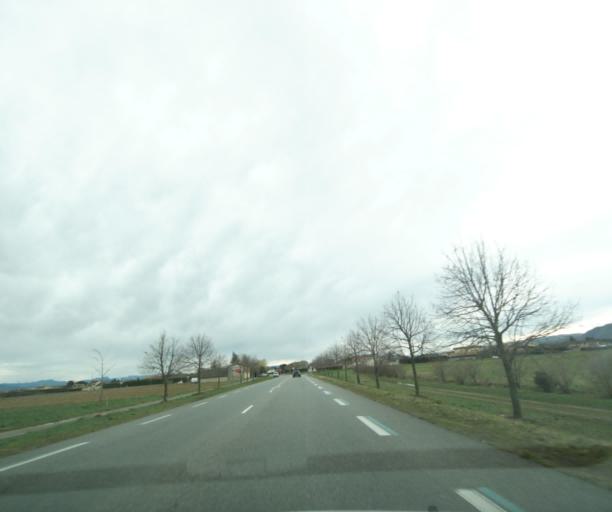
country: FR
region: Rhone-Alpes
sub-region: Departement de la Drome
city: Bourg-les-Valence
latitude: 44.9626
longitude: 4.9098
